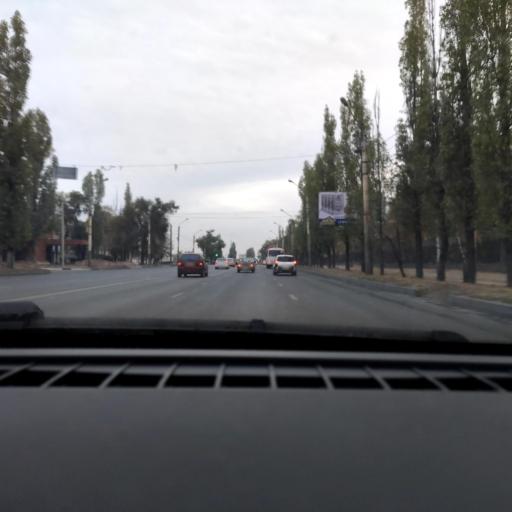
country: RU
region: Voronezj
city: Voronezh
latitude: 51.6248
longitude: 39.2326
